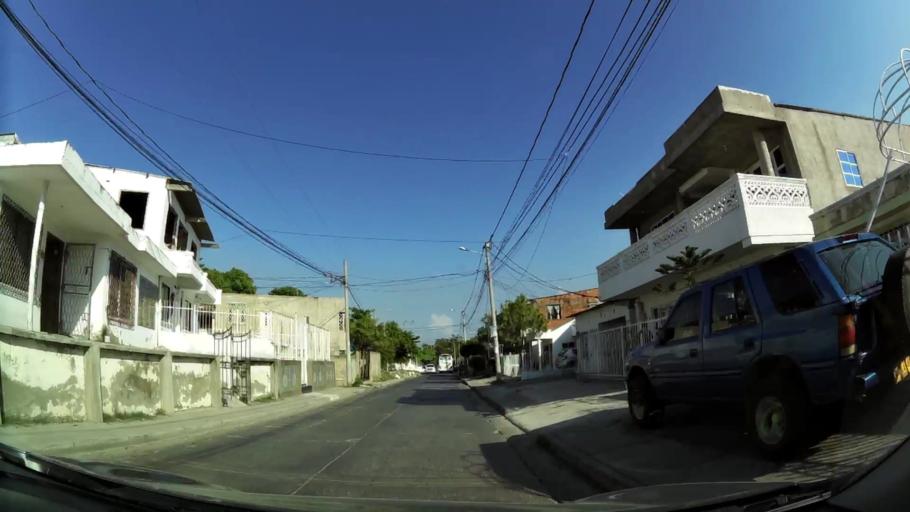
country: CO
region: Bolivar
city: Cartagena
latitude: 10.3816
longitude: -75.4852
